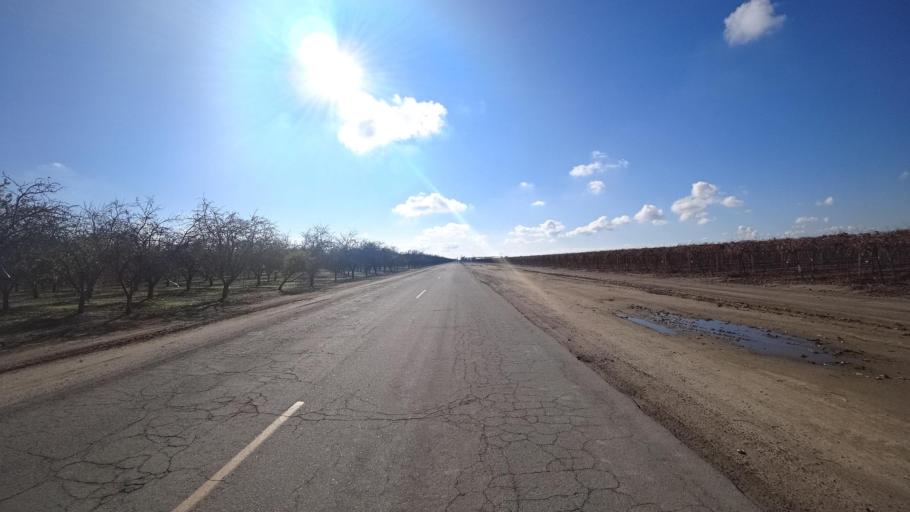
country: US
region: California
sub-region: Kern County
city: McFarland
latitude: 35.7160
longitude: -119.2586
